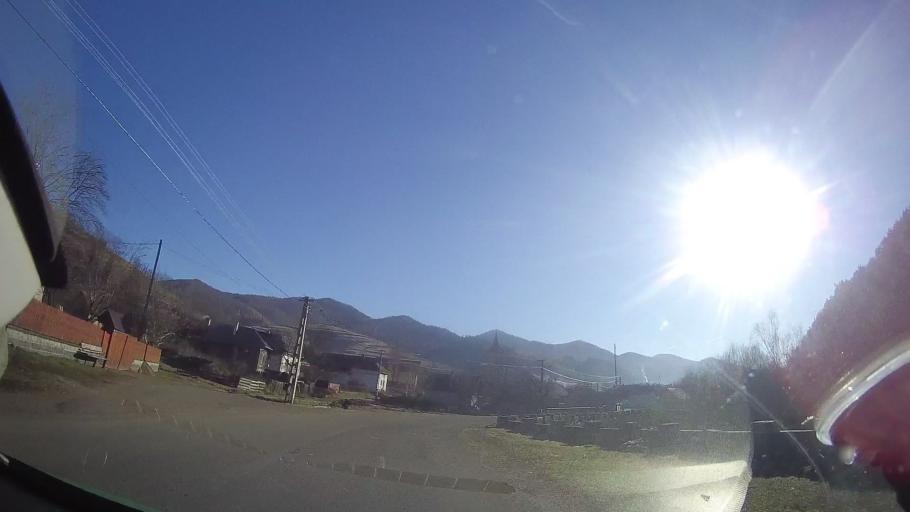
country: RO
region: Cluj
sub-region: Comuna Sacueu
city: Sacuieu
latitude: 46.8239
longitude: 22.8858
